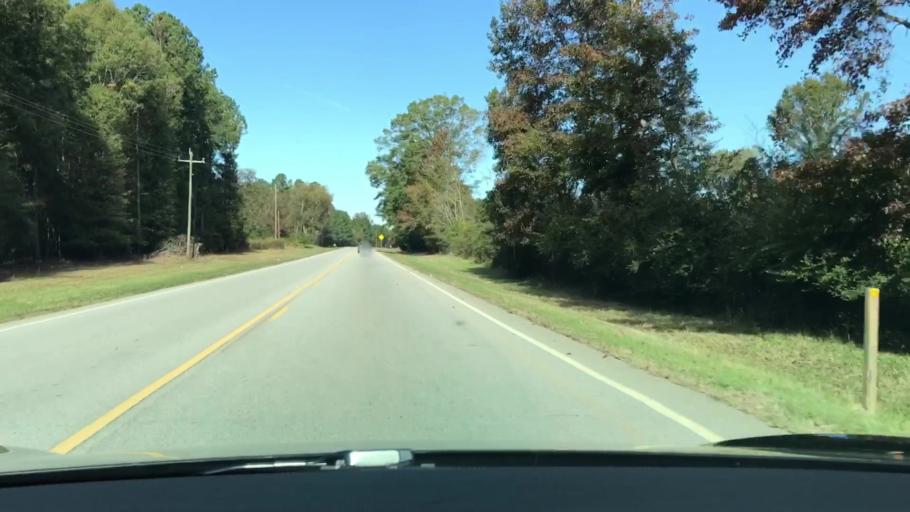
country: US
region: Georgia
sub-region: Warren County
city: Firing Range
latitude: 33.4359
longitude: -82.6890
